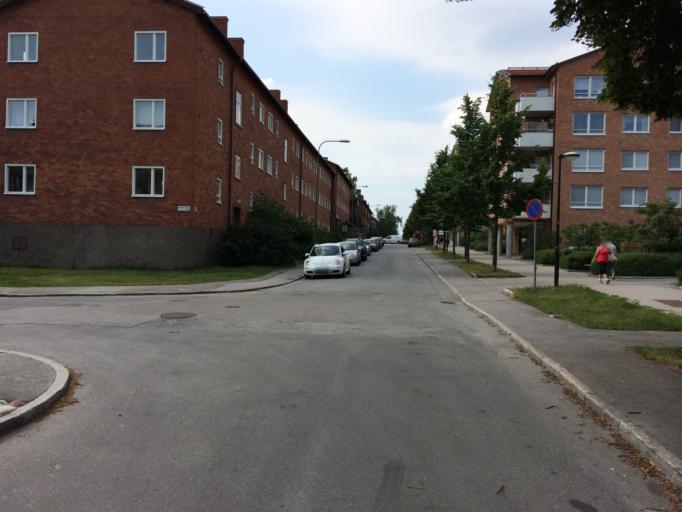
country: SE
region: Stockholm
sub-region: Huddinge Kommun
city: Segeltorp
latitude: 59.2965
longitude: 17.9850
